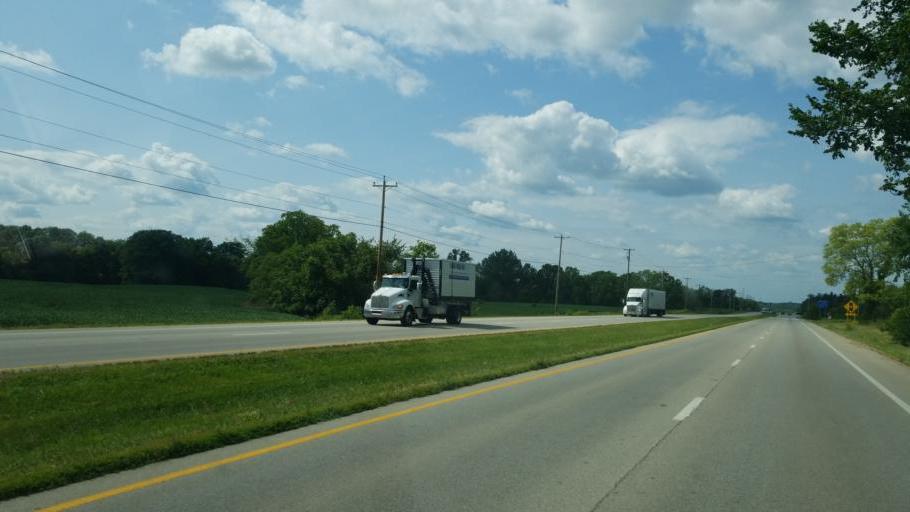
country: US
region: Ohio
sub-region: Delaware County
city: Lewis Center
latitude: 40.2379
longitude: -83.0471
